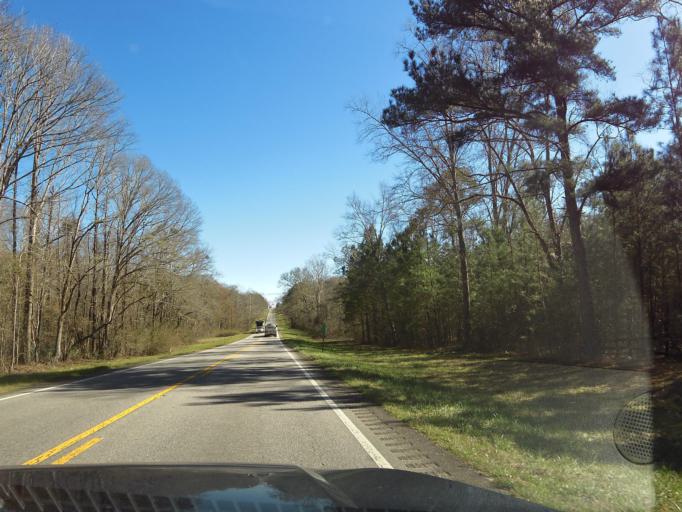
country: US
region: Alabama
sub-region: Bullock County
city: Union Springs
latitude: 32.0844
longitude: -85.5392
